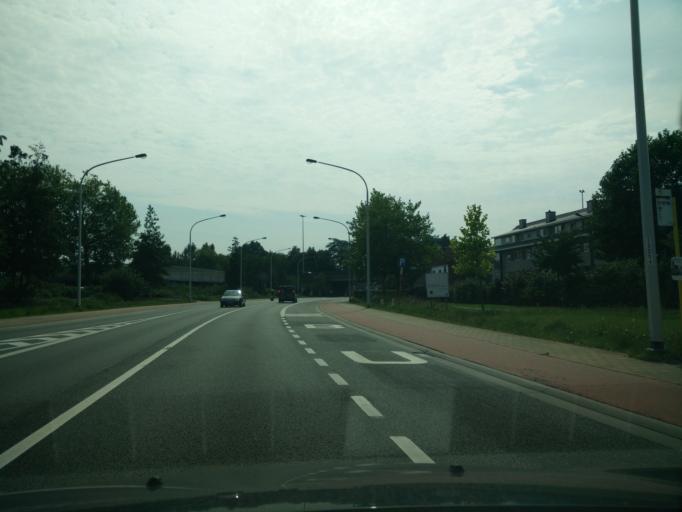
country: BE
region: Flanders
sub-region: Provincie Oost-Vlaanderen
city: Merelbeke
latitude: 51.0053
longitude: 3.7517
